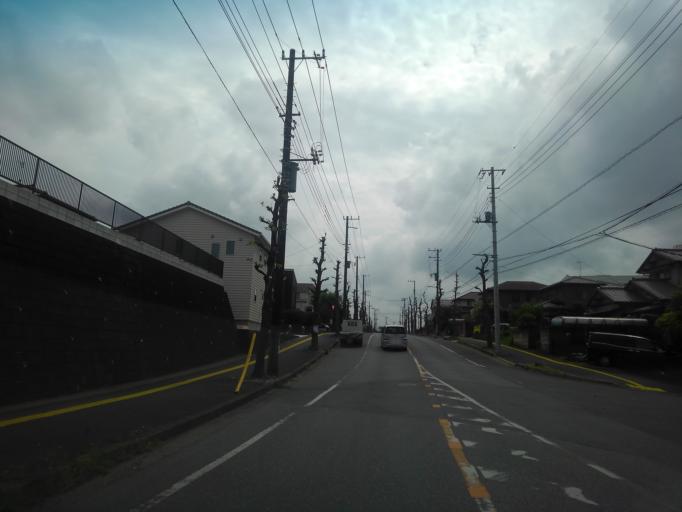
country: JP
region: Chiba
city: Kimitsu
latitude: 35.3312
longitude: 139.9159
